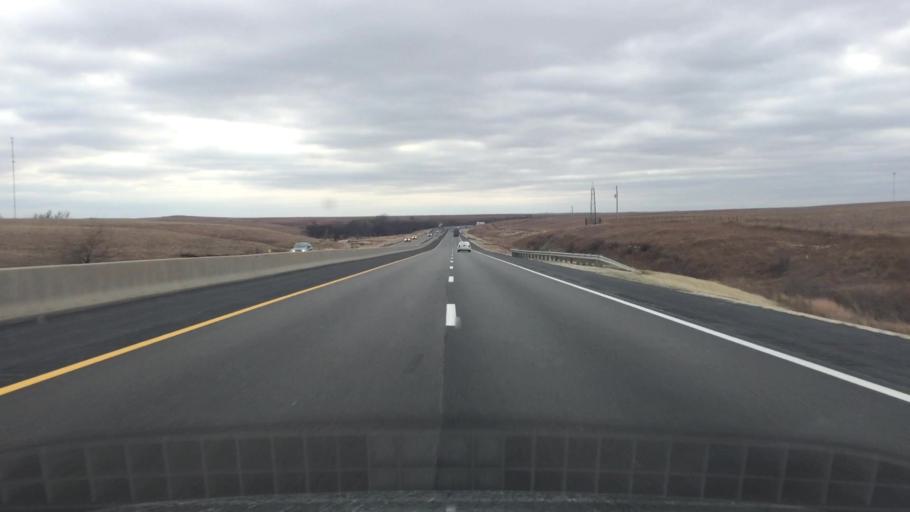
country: US
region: Kansas
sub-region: Chase County
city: Cottonwood Falls
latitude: 38.1579
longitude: -96.4877
